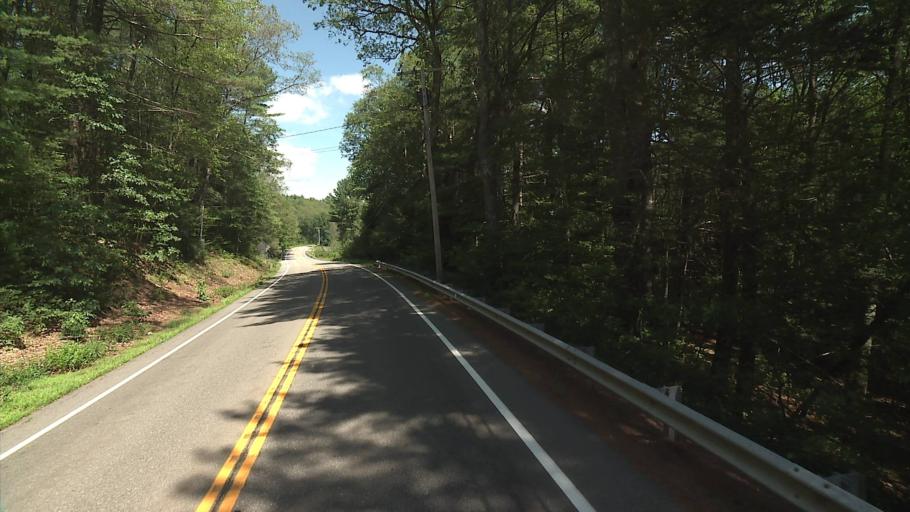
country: US
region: Massachusetts
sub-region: Worcester County
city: Southbridge
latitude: 41.9834
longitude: -72.0819
